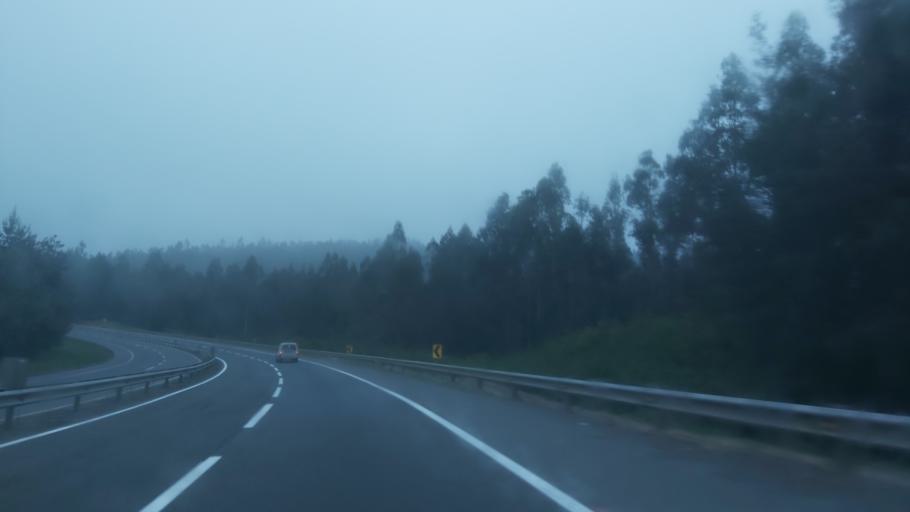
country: CL
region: Biobio
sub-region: Provincia de Concepcion
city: Penco
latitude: -36.7385
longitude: -72.8994
